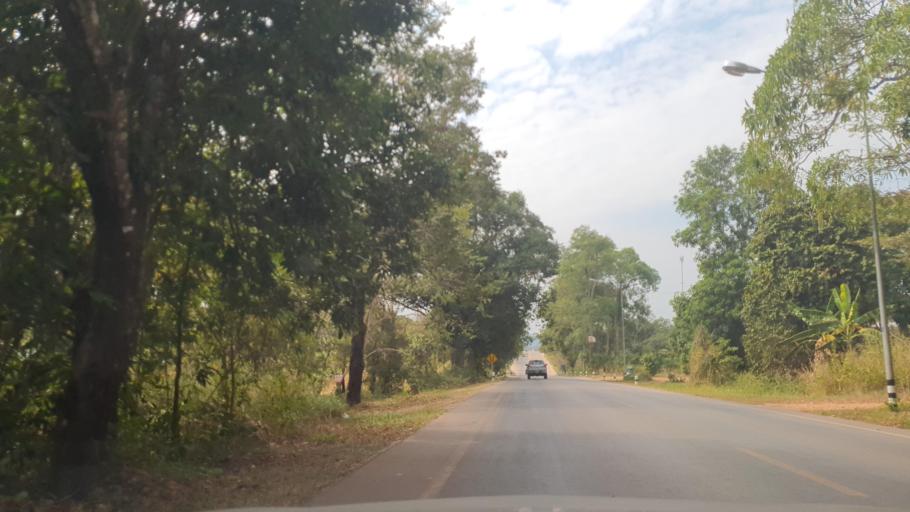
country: TH
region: Changwat Bueng Kan
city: Bung Khla
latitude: 18.2781
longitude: 103.8636
